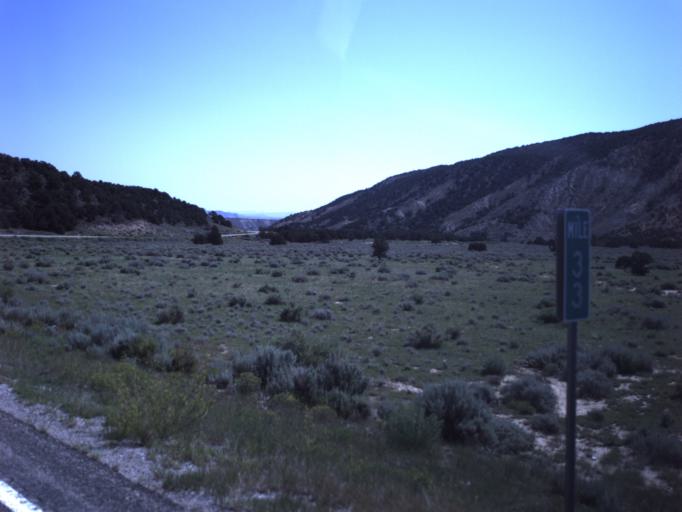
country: US
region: Utah
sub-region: Emery County
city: Ferron
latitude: 38.7514
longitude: -111.3890
